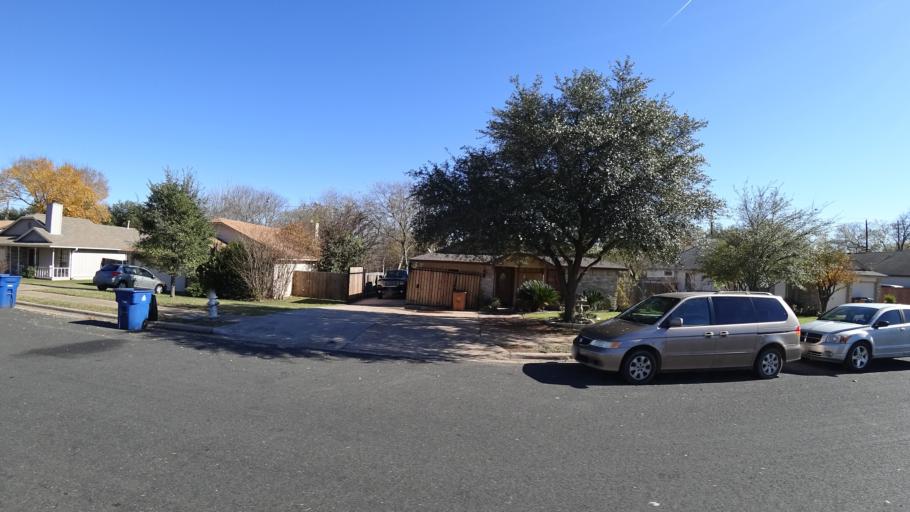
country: US
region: Texas
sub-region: Travis County
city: Wells Branch
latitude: 30.4213
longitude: -97.6880
